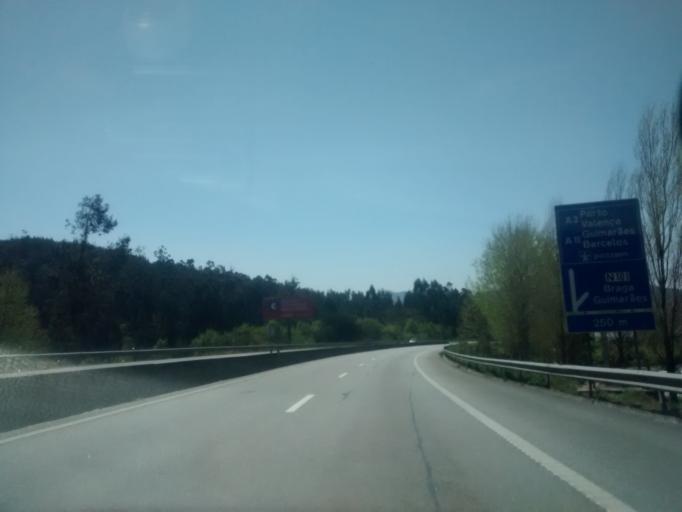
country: PT
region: Braga
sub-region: Braga
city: Braga
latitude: 41.5265
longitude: -8.4150
